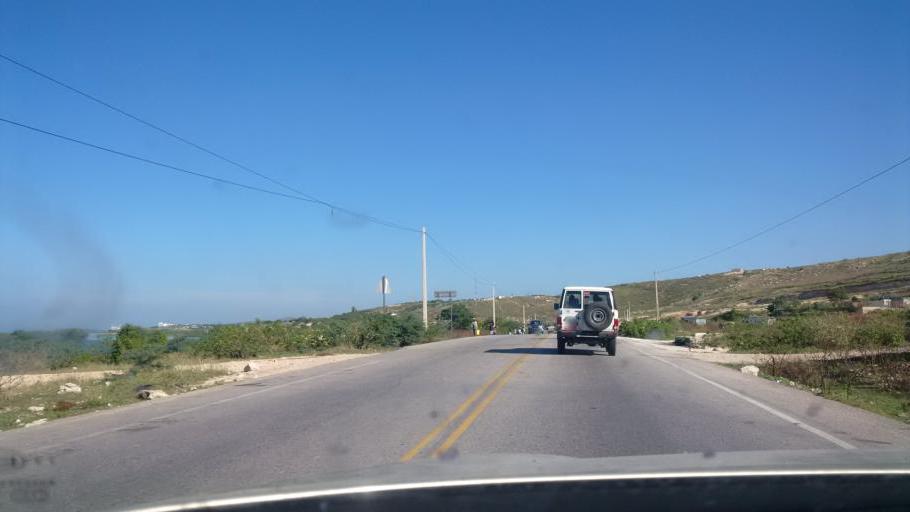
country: HT
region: Ouest
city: Cabaret
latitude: 18.6776
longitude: -72.3188
